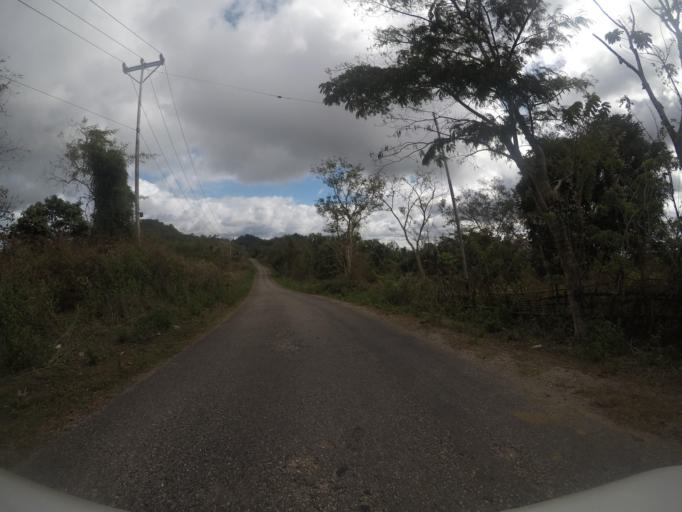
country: TL
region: Lautem
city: Lospalos
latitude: -8.5382
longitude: 126.9074
